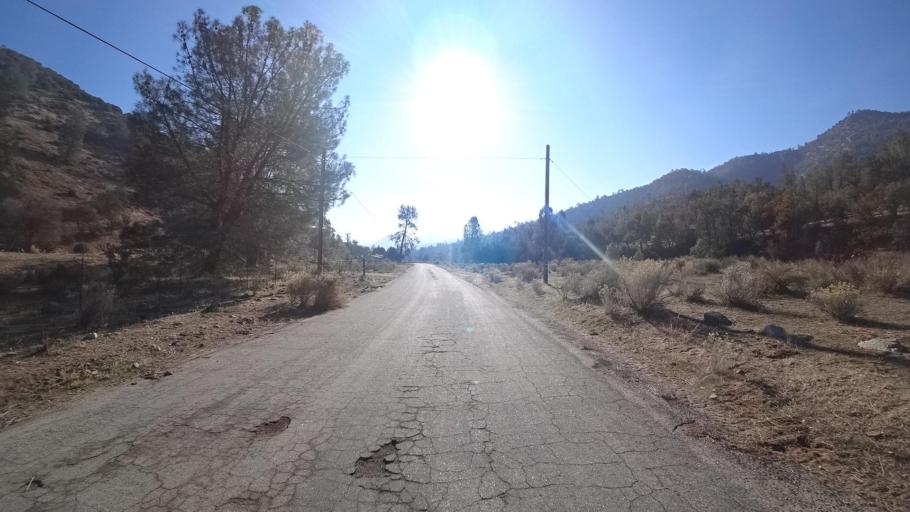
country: US
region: California
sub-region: Kern County
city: Golden Hills
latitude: 35.3009
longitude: -118.4346
